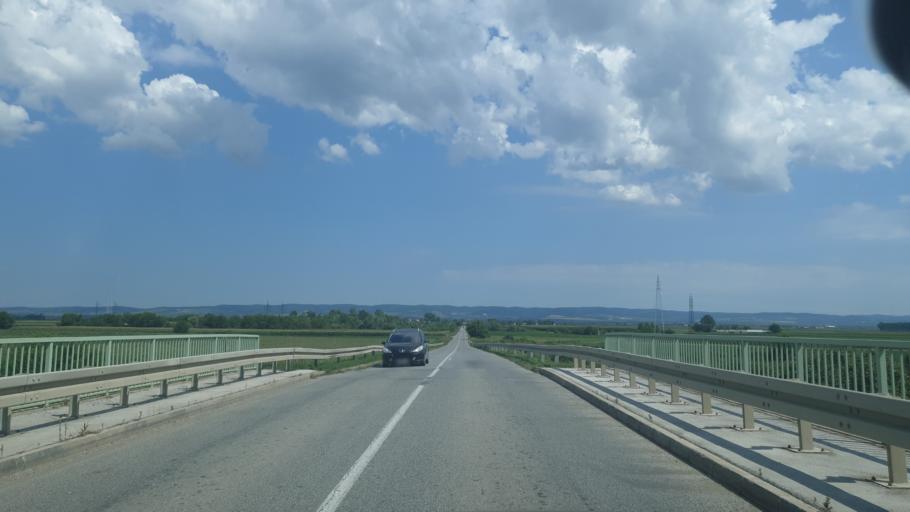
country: RS
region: Autonomna Pokrajina Vojvodina
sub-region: Sremski Okrug
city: Sremska Mitrovica
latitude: 44.9991
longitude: 19.6422
